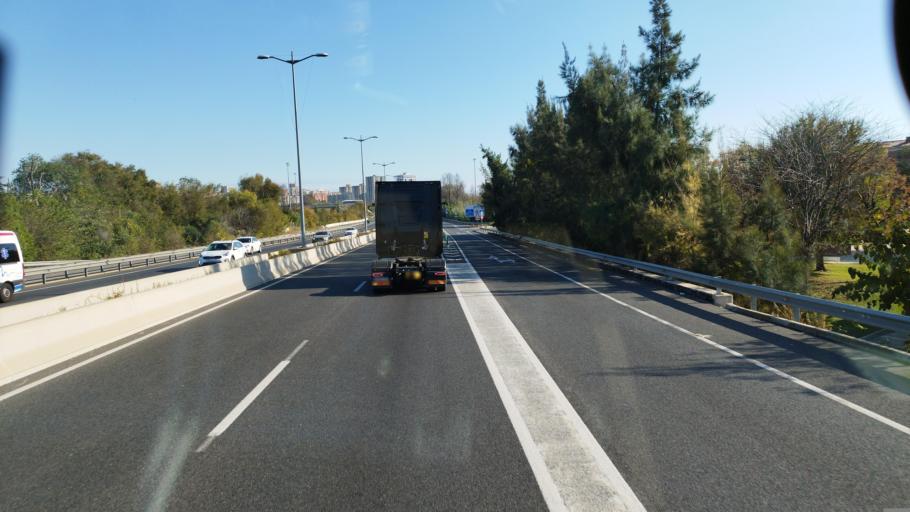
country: ES
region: Catalonia
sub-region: Provincia de Tarragona
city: Tarragona
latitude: 41.1216
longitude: 1.2236
